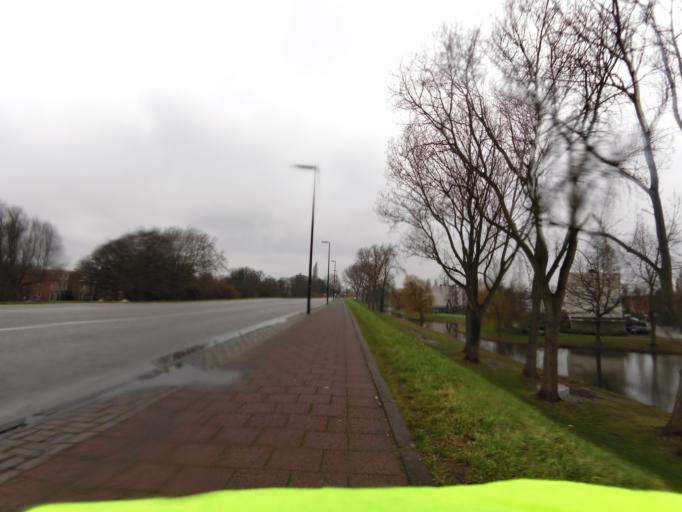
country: NL
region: South Holland
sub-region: Gemeente Vlaardingen
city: Vlaardingen
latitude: 51.9110
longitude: 4.3564
